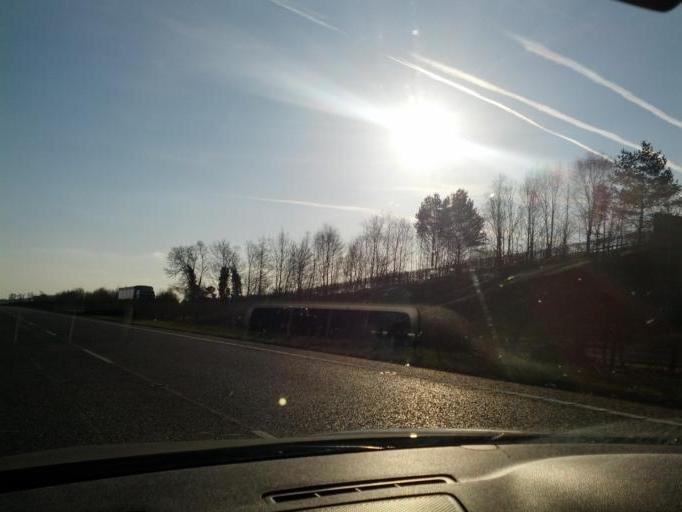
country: IE
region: Leinster
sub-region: Laois
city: Portlaoise
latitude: 53.0282
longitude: -7.2534
